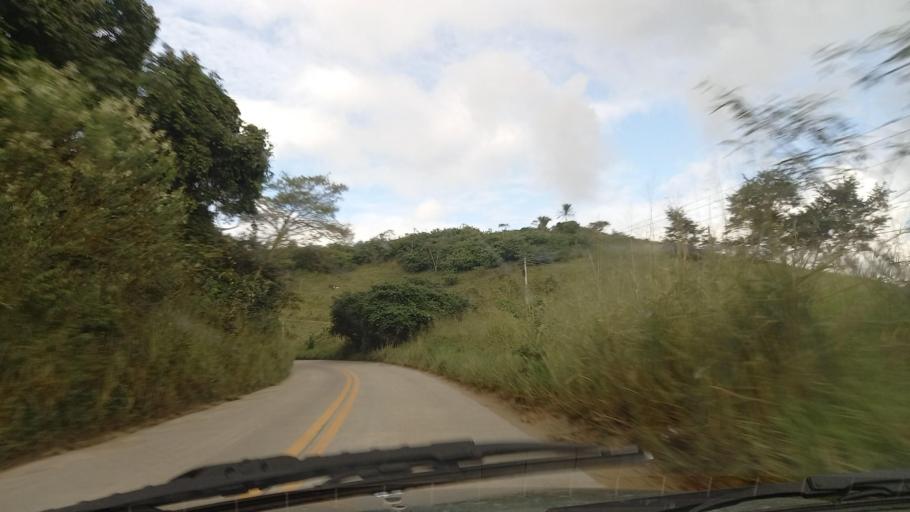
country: BR
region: Pernambuco
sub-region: Quipapa
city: Quipapa
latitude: -8.7907
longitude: -35.9815
